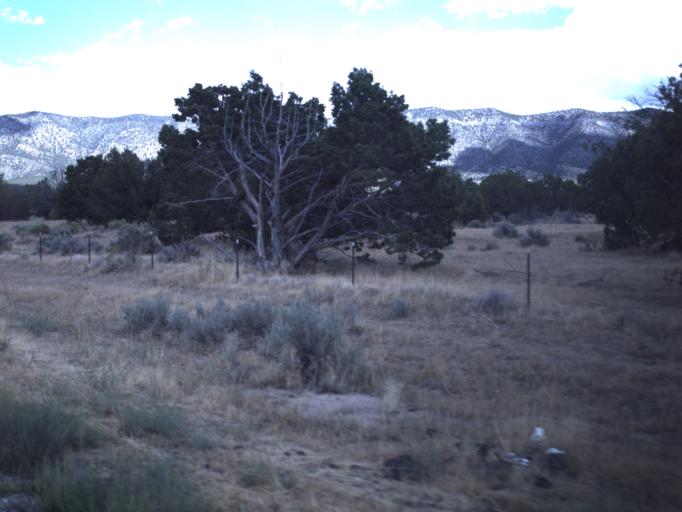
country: US
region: Utah
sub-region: Tooele County
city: Grantsville
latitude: 40.3074
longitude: -112.6413
